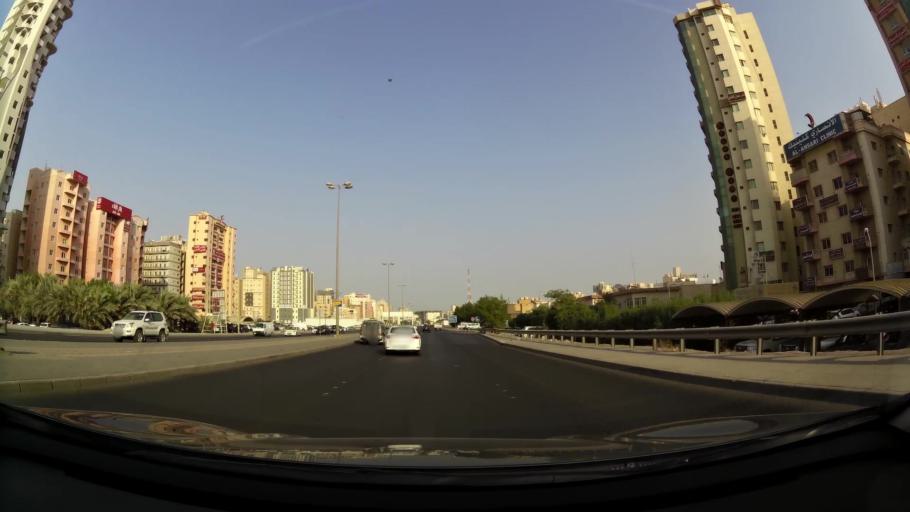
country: KW
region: Muhafazat Hawalli
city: Hawalli
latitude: 29.3316
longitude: 48.0446
